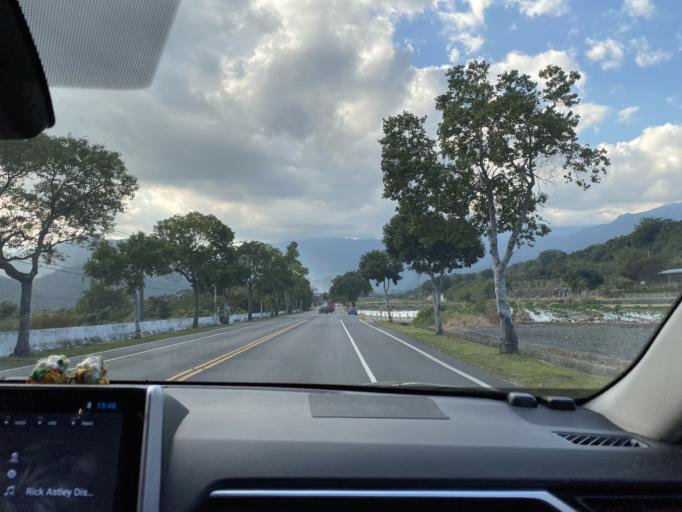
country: TW
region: Taiwan
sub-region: Taitung
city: Taitung
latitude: 22.8936
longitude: 121.1332
